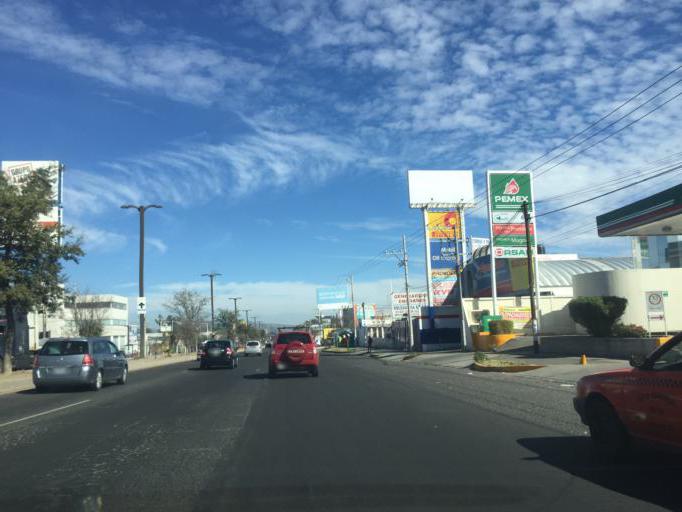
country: MX
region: Queretaro
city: San Juan del Rio
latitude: 20.3882
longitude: -99.9844
